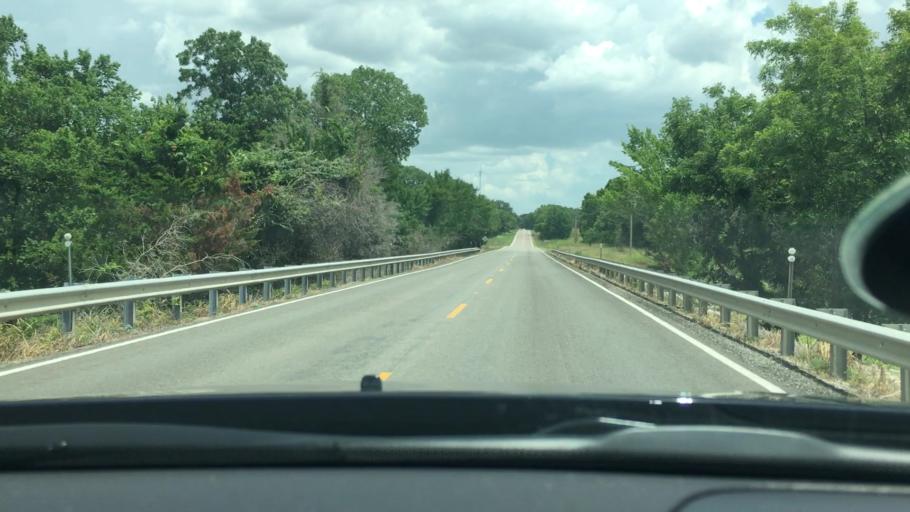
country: US
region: Texas
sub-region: Grayson County
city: Sherwood Shores
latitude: 33.9837
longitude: -96.8992
